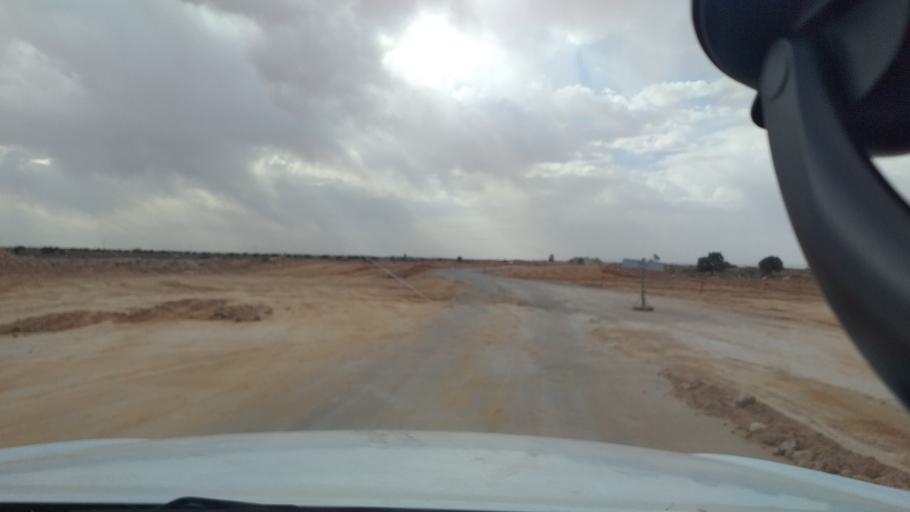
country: TN
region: Madanin
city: Medenine
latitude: 33.3068
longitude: 10.6133
